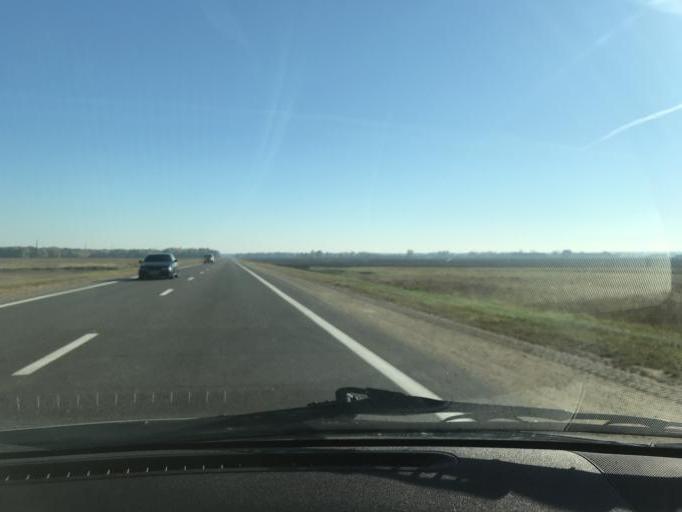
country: BY
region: Brest
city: Ivanava
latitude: 52.1560
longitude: 25.6751
